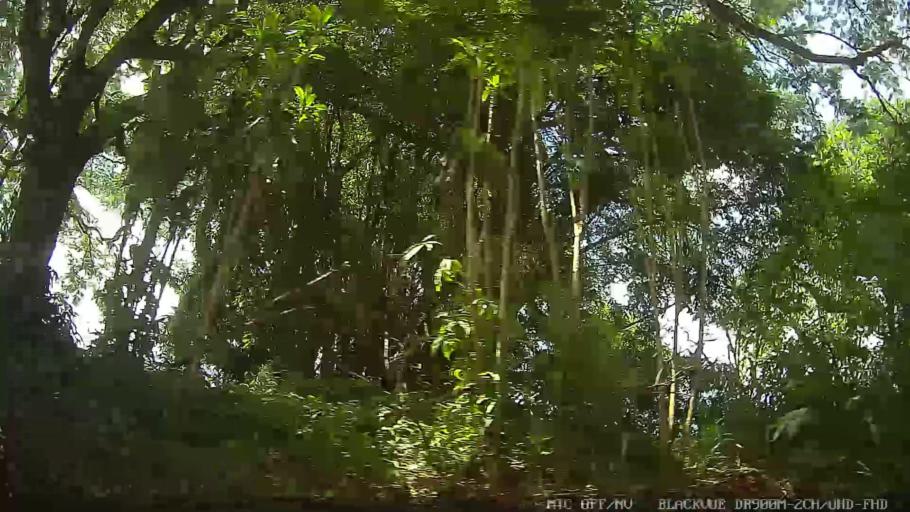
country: BR
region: Sao Paulo
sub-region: Artur Nogueira
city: Artur Nogueira
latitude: -22.5873
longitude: -47.0768
